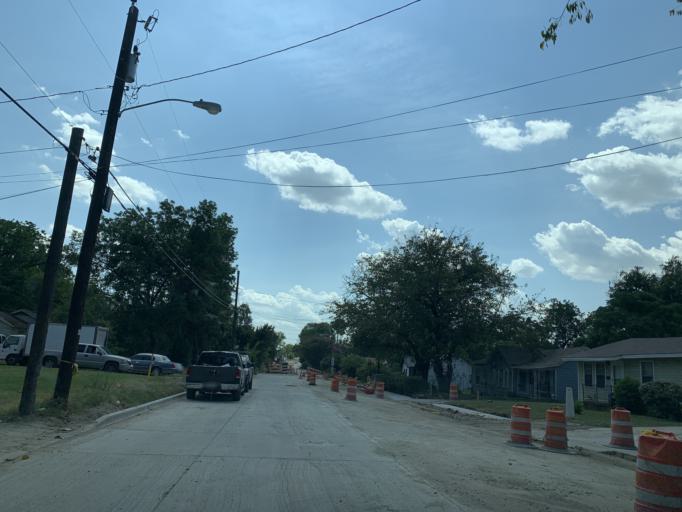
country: US
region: Texas
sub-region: Dallas County
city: Dallas
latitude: 32.7116
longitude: -96.7719
